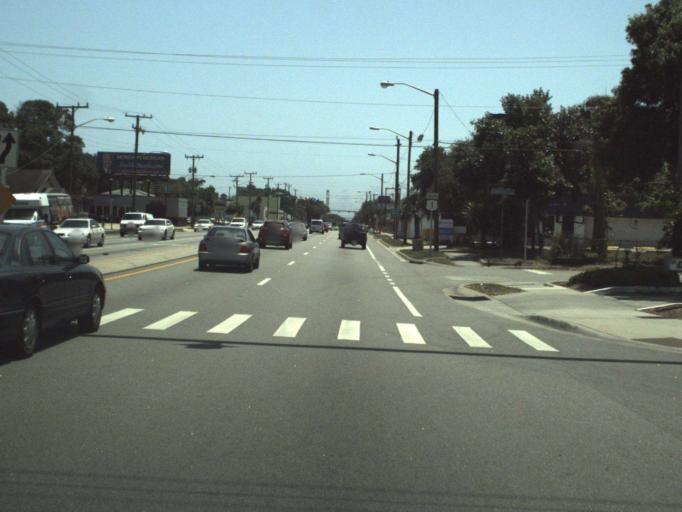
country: US
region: Florida
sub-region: Volusia County
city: Daytona Beach
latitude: 29.2265
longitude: -81.0313
